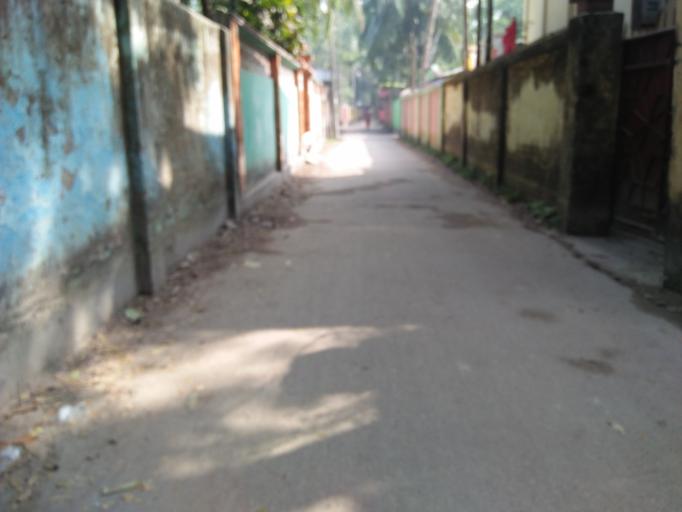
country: BD
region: Barisal
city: Bhola
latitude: 22.6805
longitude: 90.6391
